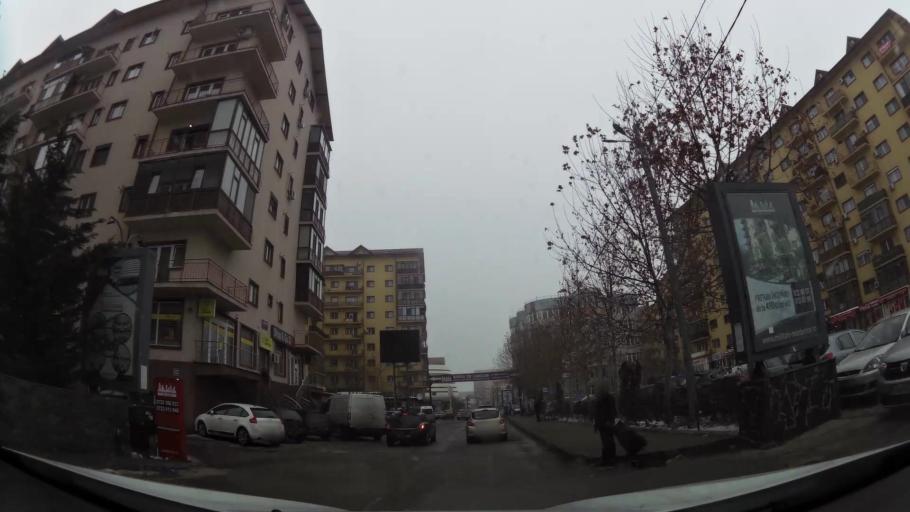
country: RO
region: Ilfov
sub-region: Comuna Chiajna
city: Chiajna
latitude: 44.4421
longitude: 25.9873
